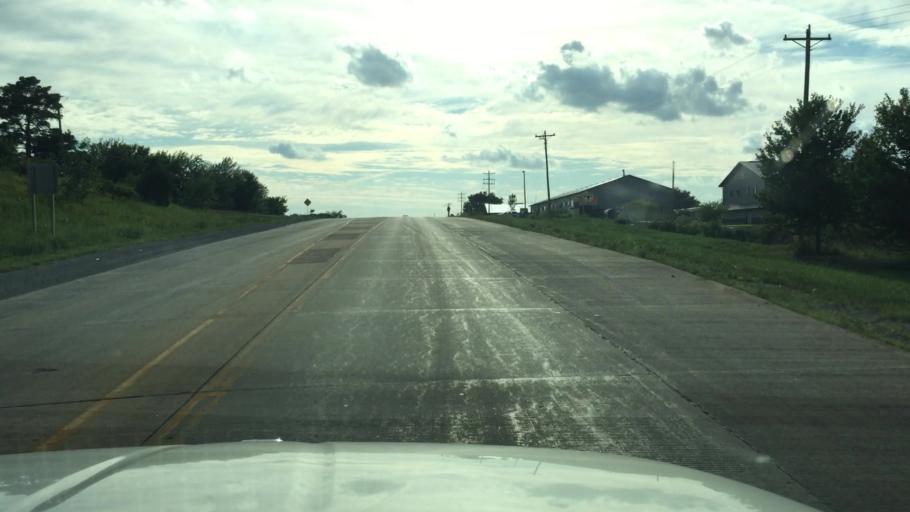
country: US
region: Iowa
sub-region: Johnson County
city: Iowa City
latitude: 41.6710
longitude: -91.4508
